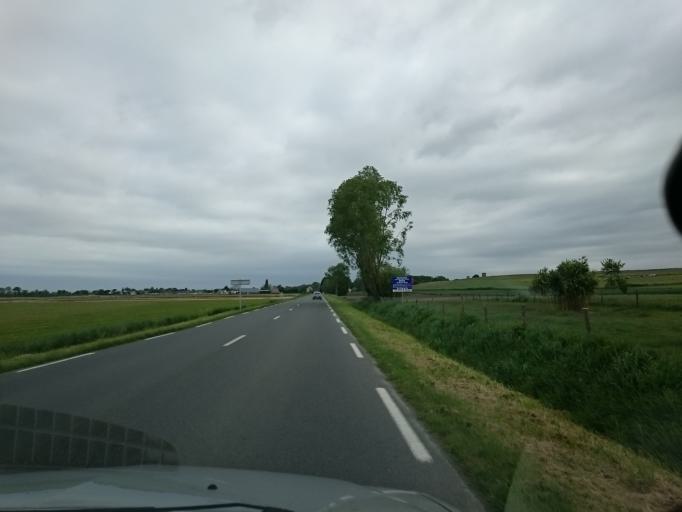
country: FR
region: Lower Normandy
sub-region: Departement de la Manche
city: Pontorson
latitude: 48.5847
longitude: -1.5112
